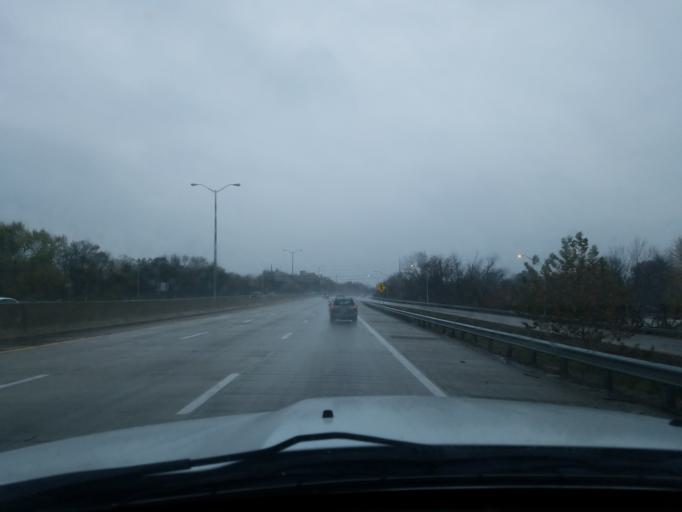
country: US
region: Kentucky
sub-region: Jefferson County
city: Shively
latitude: 38.2053
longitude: -85.8279
